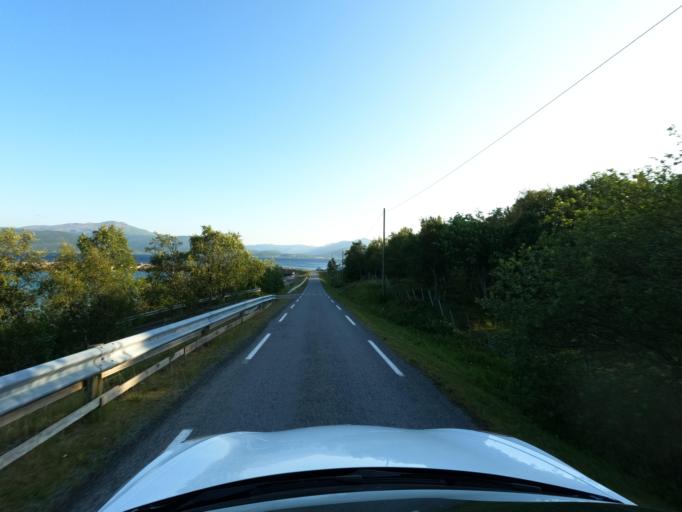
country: NO
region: Troms
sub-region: Skanland
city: Evenskjer
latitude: 68.4576
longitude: 16.6935
